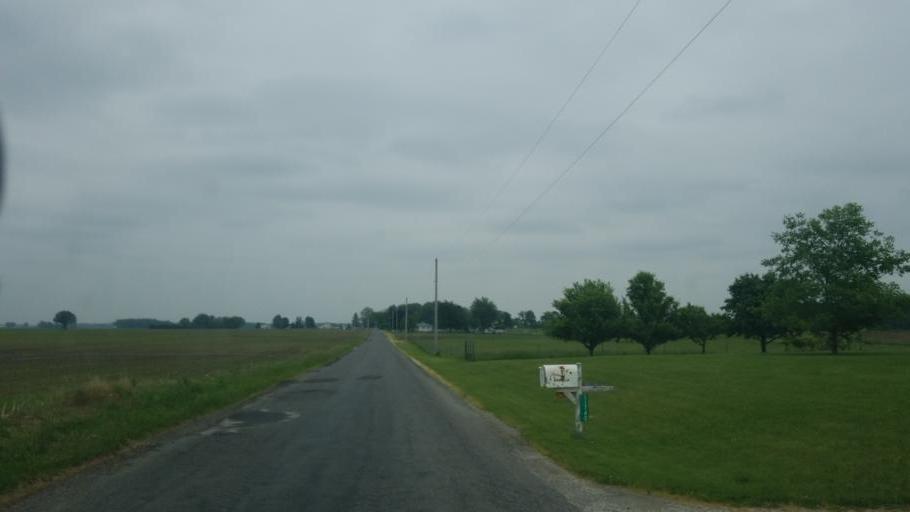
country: US
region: Indiana
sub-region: Marshall County
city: Bremen
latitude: 41.4935
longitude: -86.0926
